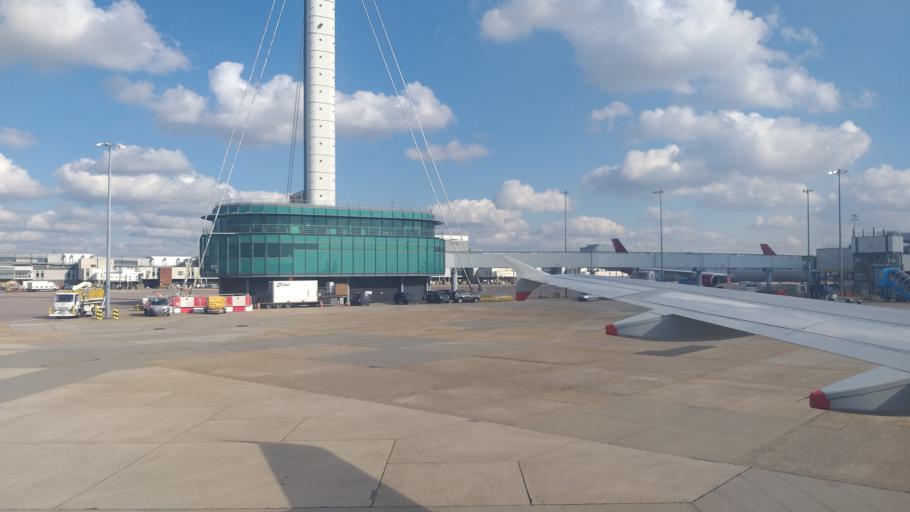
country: GB
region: England
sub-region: Greater London
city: West Drayton
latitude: 51.4716
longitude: -0.4673
